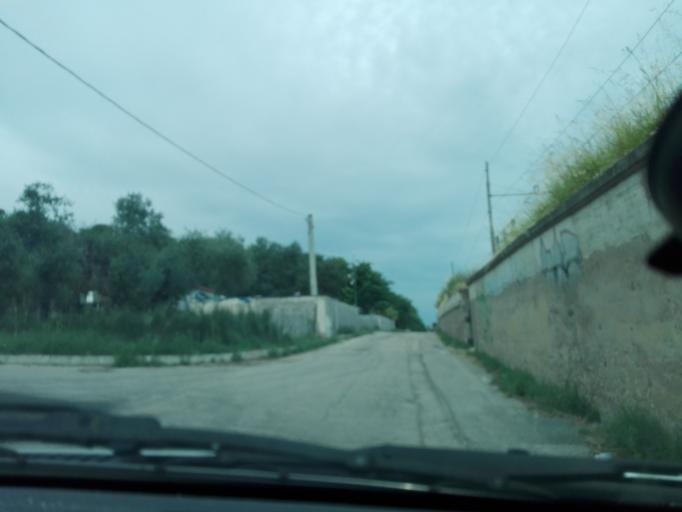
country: IT
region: Abruzzo
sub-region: Provincia di Pescara
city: Montesilvano Marina
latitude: 42.5015
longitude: 14.1634
